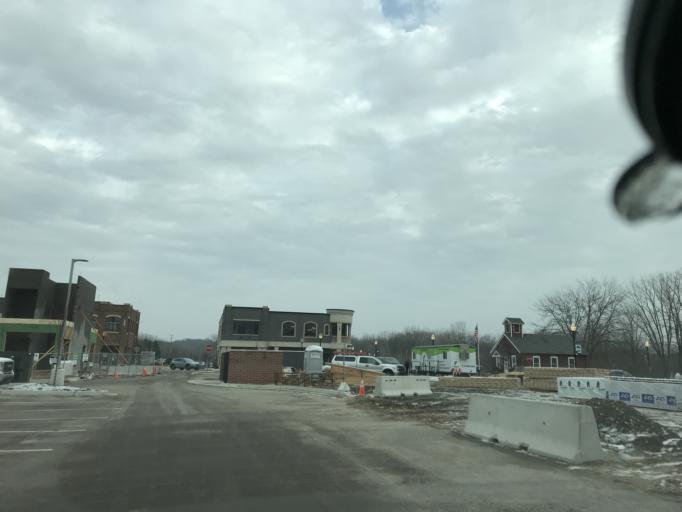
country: US
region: Michigan
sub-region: Kent County
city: Forest Hills
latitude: 42.9546
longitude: -85.4854
